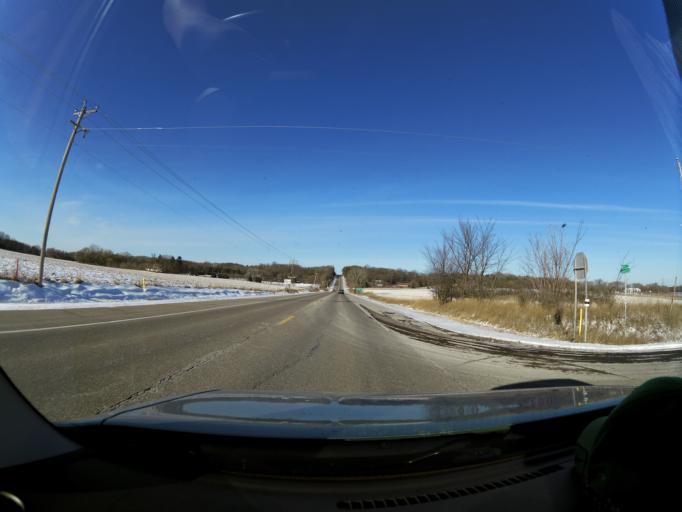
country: US
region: Minnesota
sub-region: Washington County
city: Afton
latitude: 44.9164
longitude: -92.8625
